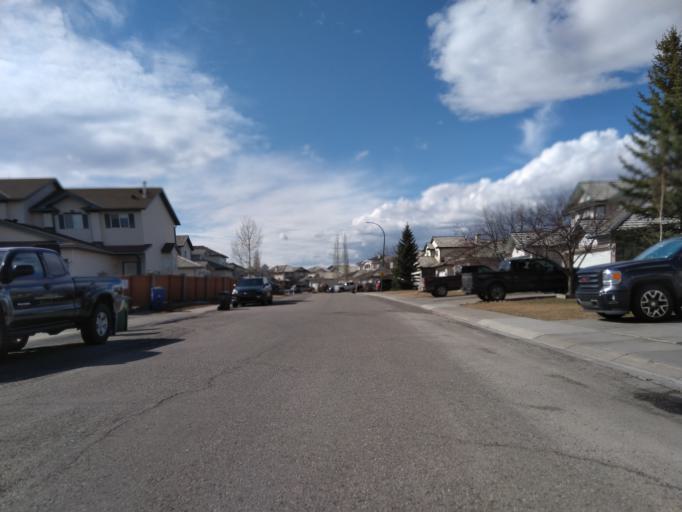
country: CA
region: Alberta
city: Cochrane
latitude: 51.1879
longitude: -114.5110
